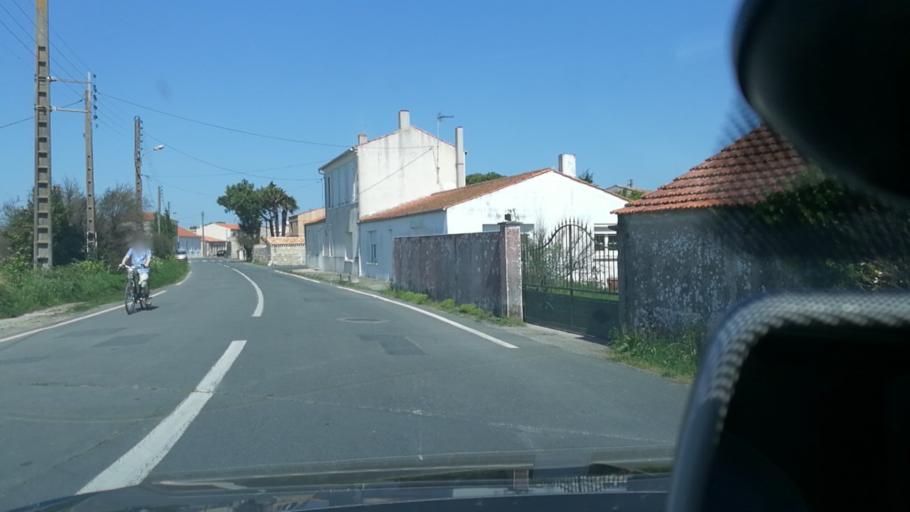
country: FR
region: Poitou-Charentes
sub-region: Departement de la Charente-Maritime
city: Saint-Trojan-les-Bains
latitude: 45.8716
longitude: -1.2173
